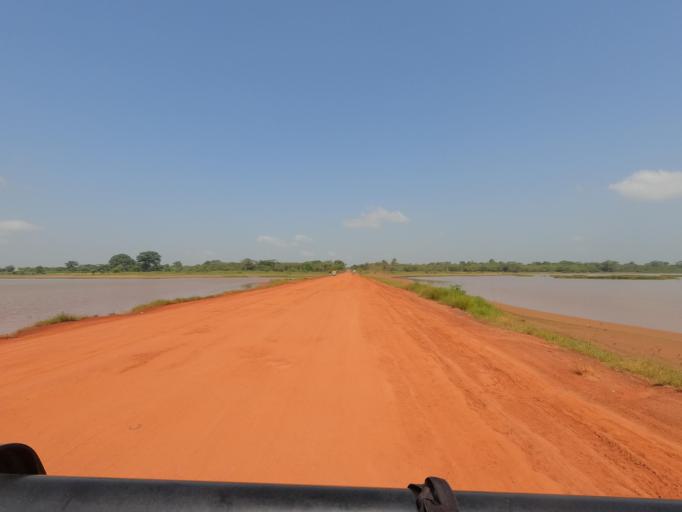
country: GW
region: Cacheu
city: Canchungo
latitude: 12.2615
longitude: -15.7835
